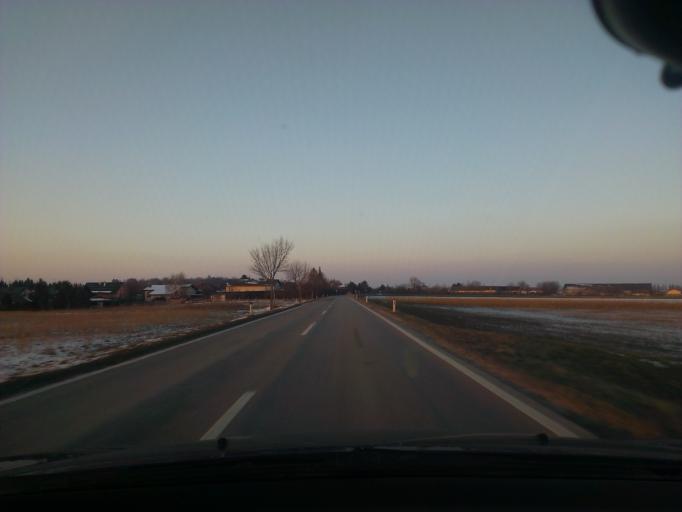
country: AT
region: Lower Austria
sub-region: Politischer Bezirk Baden
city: Reisenberg
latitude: 47.9887
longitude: 16.5183
